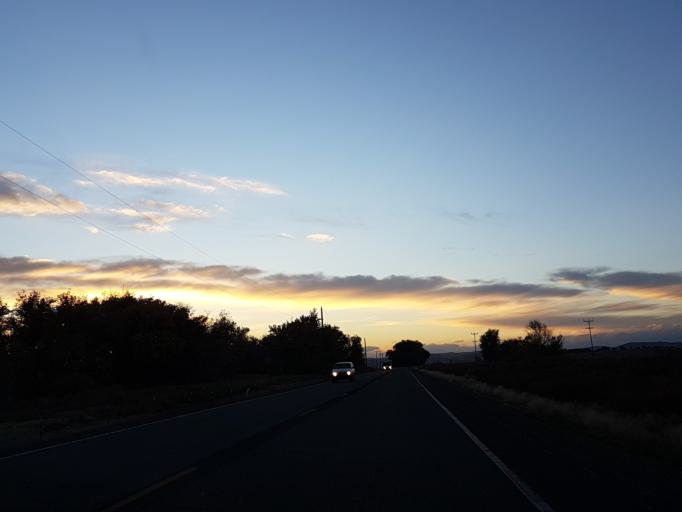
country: US
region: Oregon
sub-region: Malheur County
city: Vale
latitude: 43.9379
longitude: -117.3269
